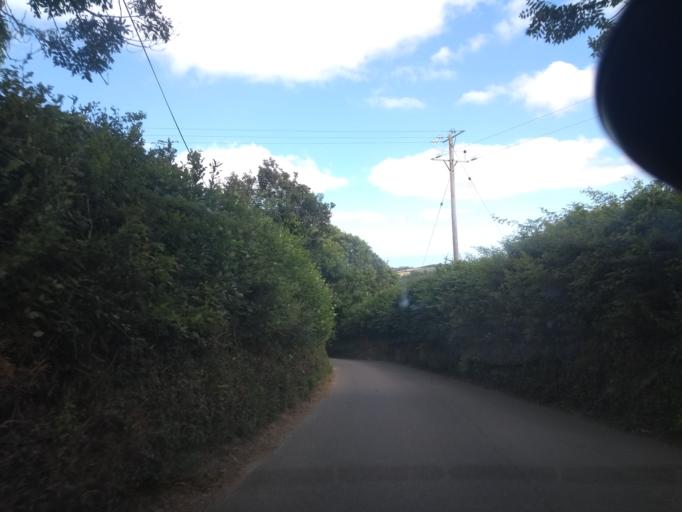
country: GB
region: England
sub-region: Devon
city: Modbury
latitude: 50.3069
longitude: -3.8572
